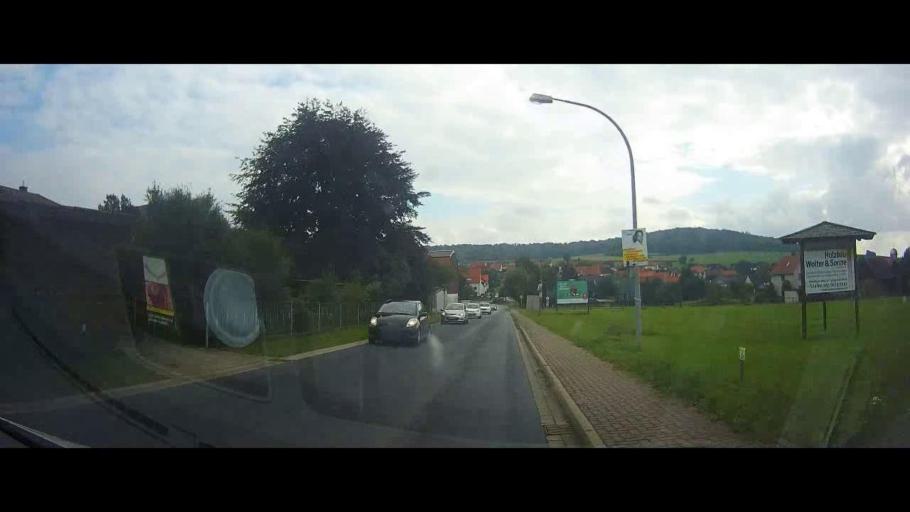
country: DE
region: Lower Saxony
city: Adelebsen
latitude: 51.5533
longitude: 9.7773
